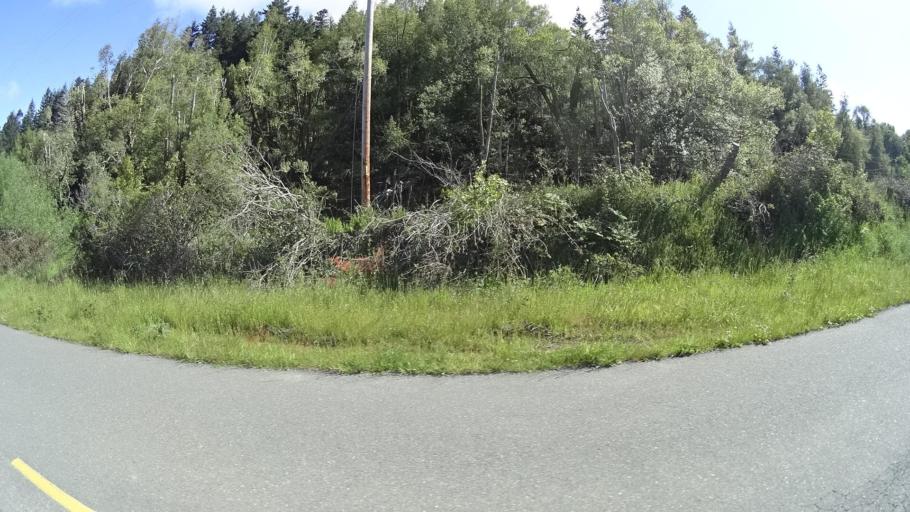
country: US
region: California
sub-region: Humboldt County
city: Ferndale
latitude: 40.3409
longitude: -124.3167
